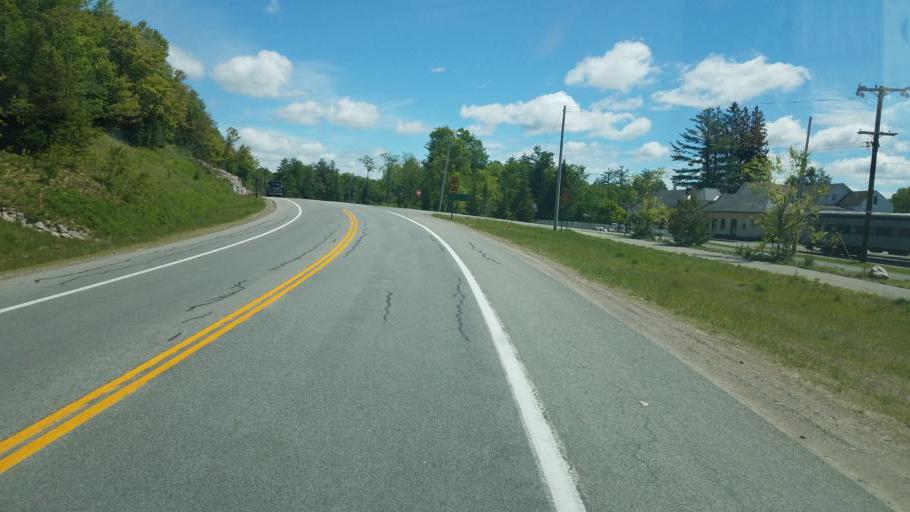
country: US
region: New York
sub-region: Oneida County
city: Boonville
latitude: 43.6985
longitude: -75.0068
